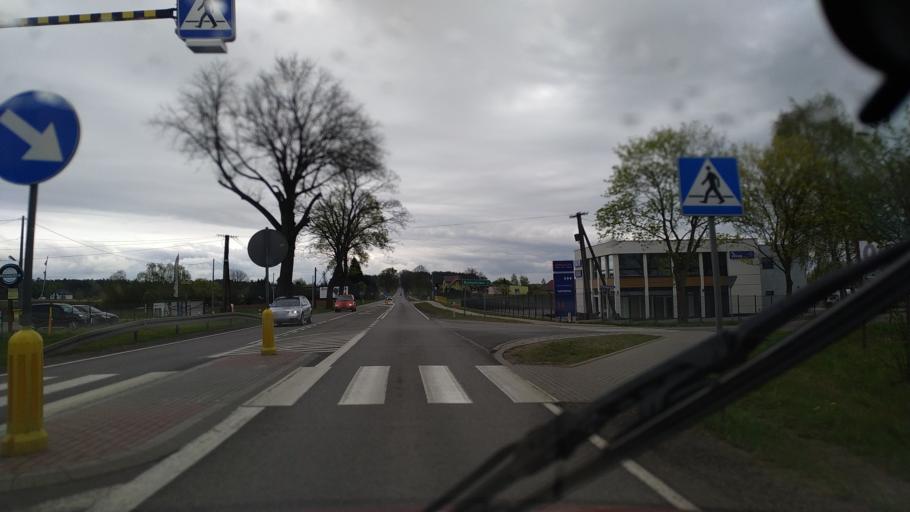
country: PL
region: Pomeranian Voivodeship
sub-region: Powiat starogardzki
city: Zblewo
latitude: 53.9327
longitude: 18.3405
